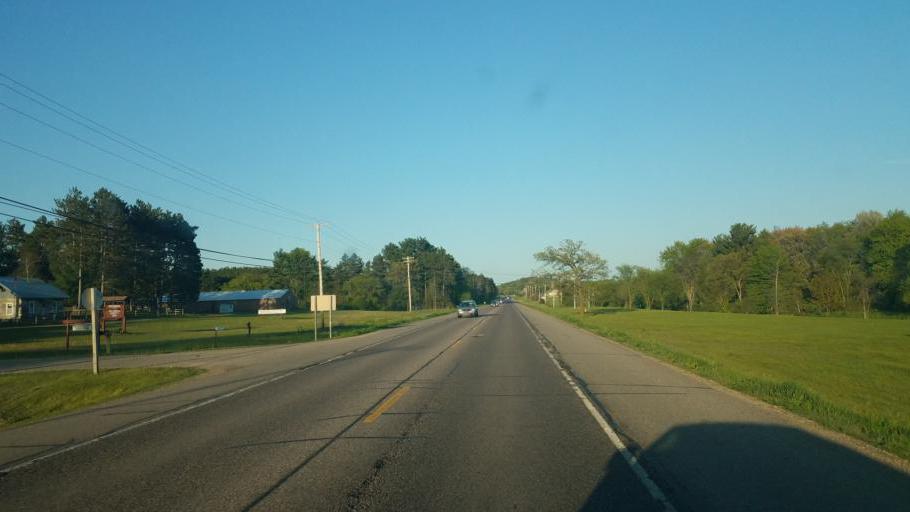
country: US
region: Wisconsin
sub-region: Sauk County
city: Reedsburg
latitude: 43.5330
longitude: -89.9281
